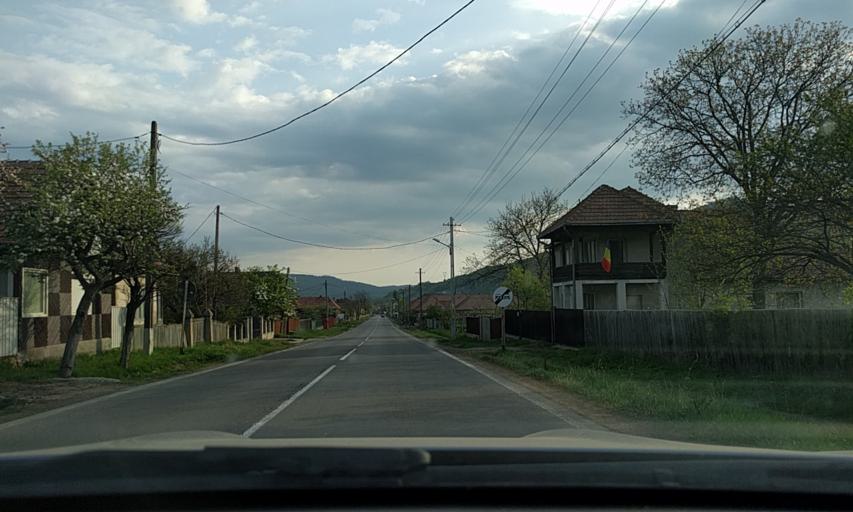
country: RO
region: Bacau
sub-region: Oras Slanic-Moldova
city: Slanic-Moldova
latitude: 46.1399
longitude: 26.4529
